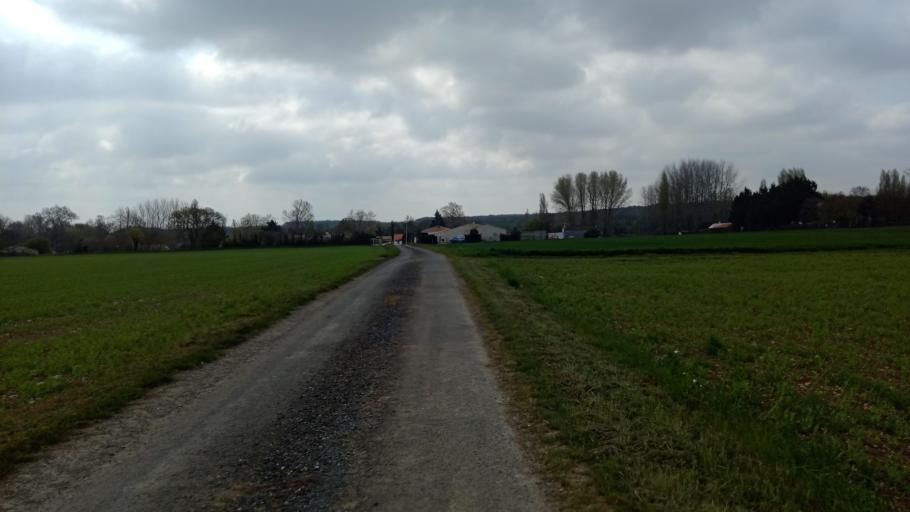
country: FR
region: Poitou-Charentes
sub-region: Departement de la Charente-Maritime
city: Verines
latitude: 46.1565
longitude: -0.9341
